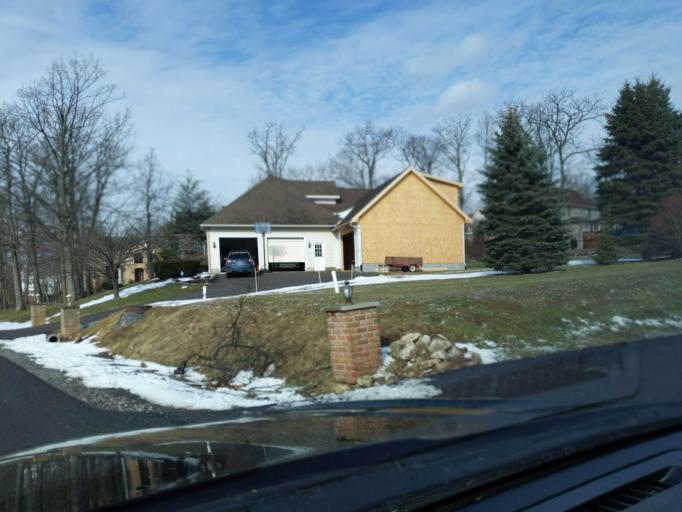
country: US
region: Pennsylvania
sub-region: Blair County
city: Lakemont
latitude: 40.4719
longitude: -78.3766
